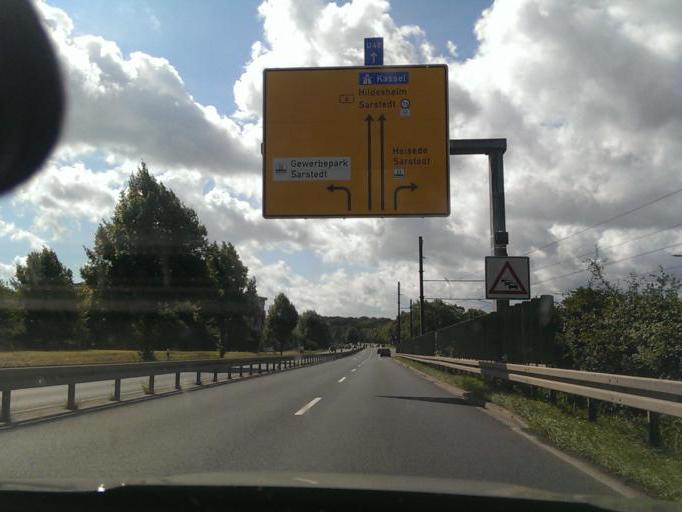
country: DE
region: Lower Saxony
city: Sarstedt
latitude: 52.2558
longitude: 9.8591
